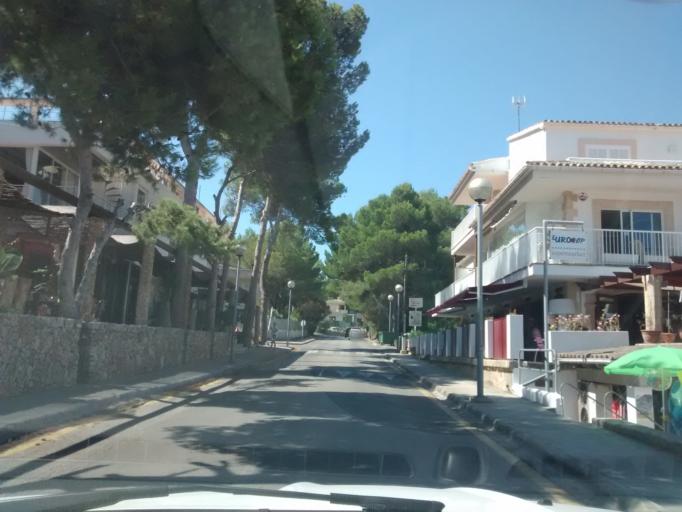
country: ES
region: Balearic Islands
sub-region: Illes Balears
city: Alcudia
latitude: 39.8645
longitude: 3.1438
